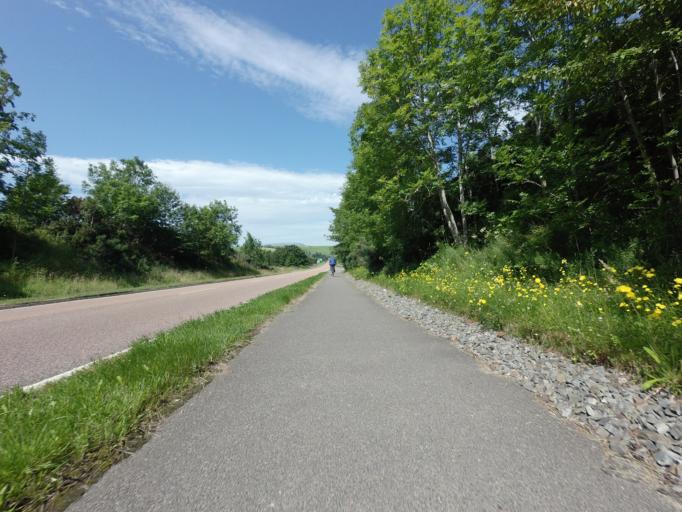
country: GB
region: Scotland
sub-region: Highland
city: Conon Bridge
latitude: 57.5707
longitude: -4.4278
